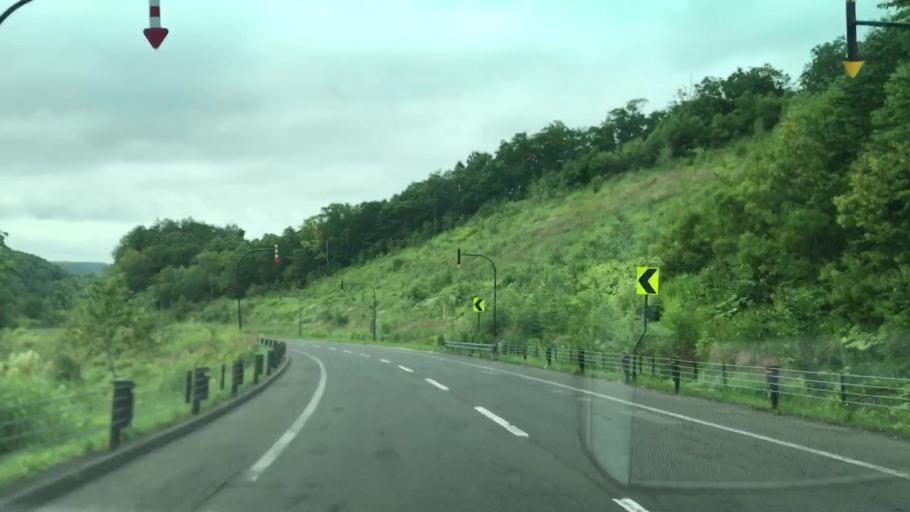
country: JP
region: Hokkaido
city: Otaru
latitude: 42.9597
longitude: 140.8718
